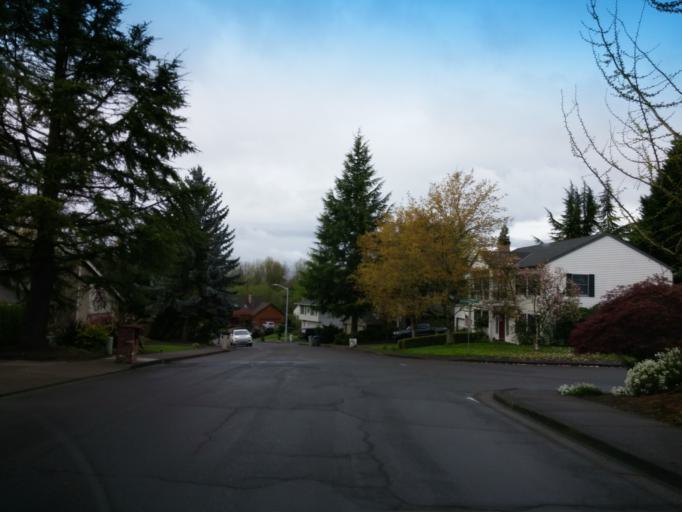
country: US
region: Oregon
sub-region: Washington County
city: Oak Hills
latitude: 45.5347
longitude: -122.8388
